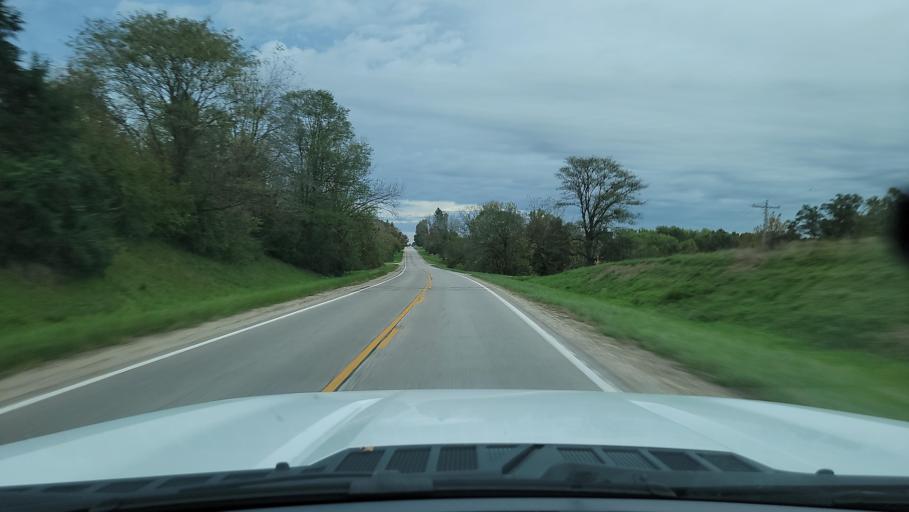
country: US
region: Illinois
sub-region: Schuyler County
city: Rushville
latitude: 40.0425
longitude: -90.6153
